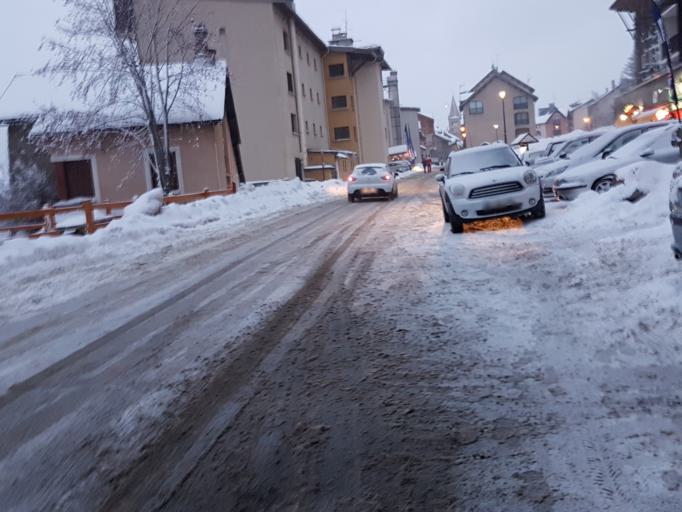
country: IT
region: Piedmont
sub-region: Provincia di Torino
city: Claviere
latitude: 44.9325
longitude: 6.7265
